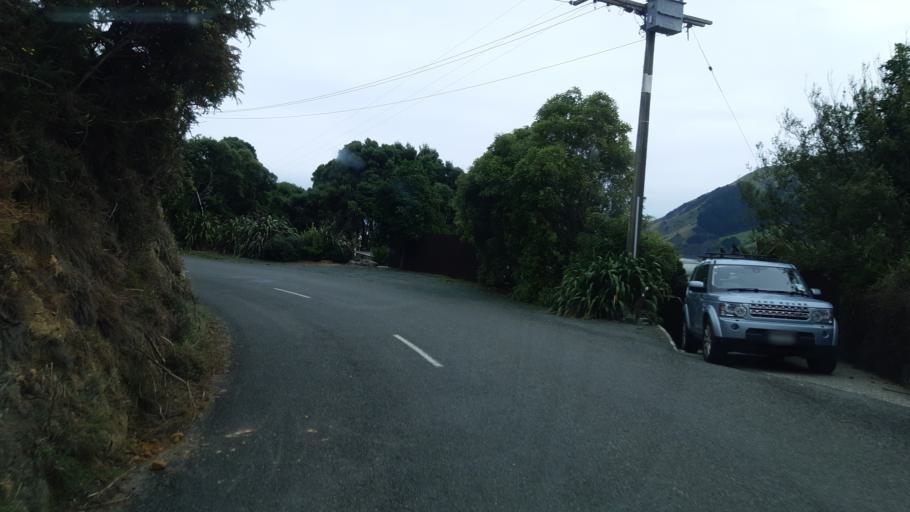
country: NZ
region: Nelson
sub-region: Nelson City
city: Nelson
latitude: -41.1668
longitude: 173.4199
